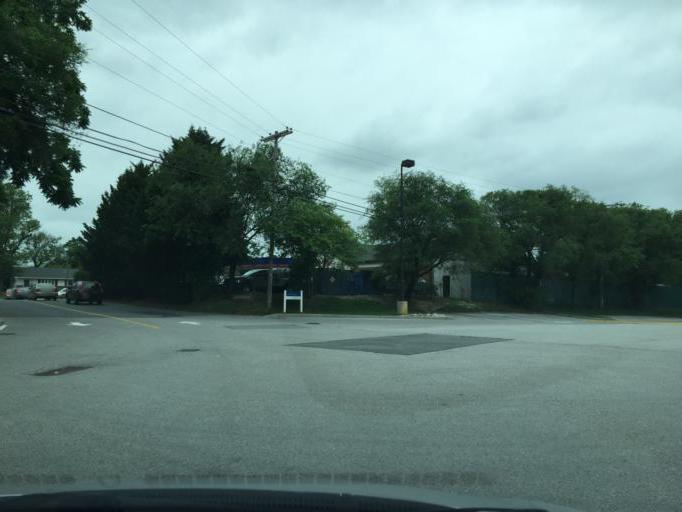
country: US
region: Maryland
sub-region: Baltimore County
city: Timonium
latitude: 39.4434
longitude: -76.6240
